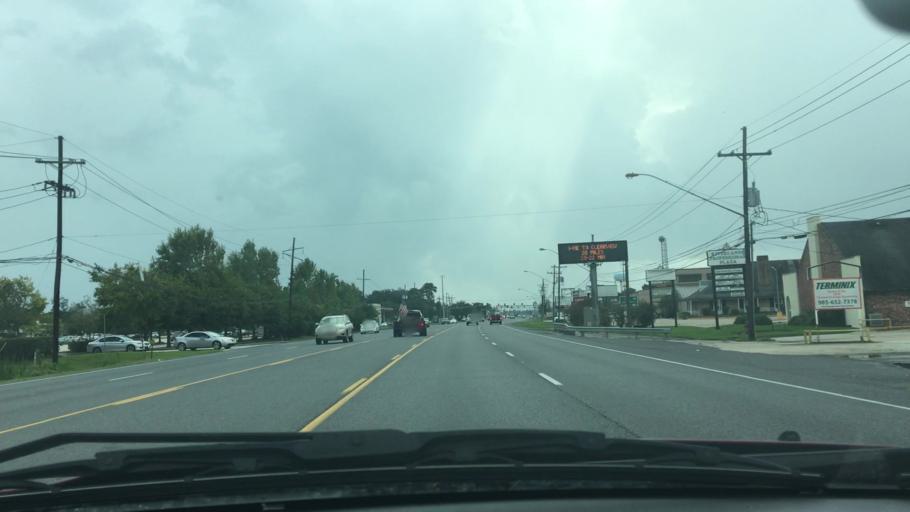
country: US
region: Louisiana
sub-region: Saint John the Baptist Parish
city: Laplace
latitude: 30.0690
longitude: -90.4847
